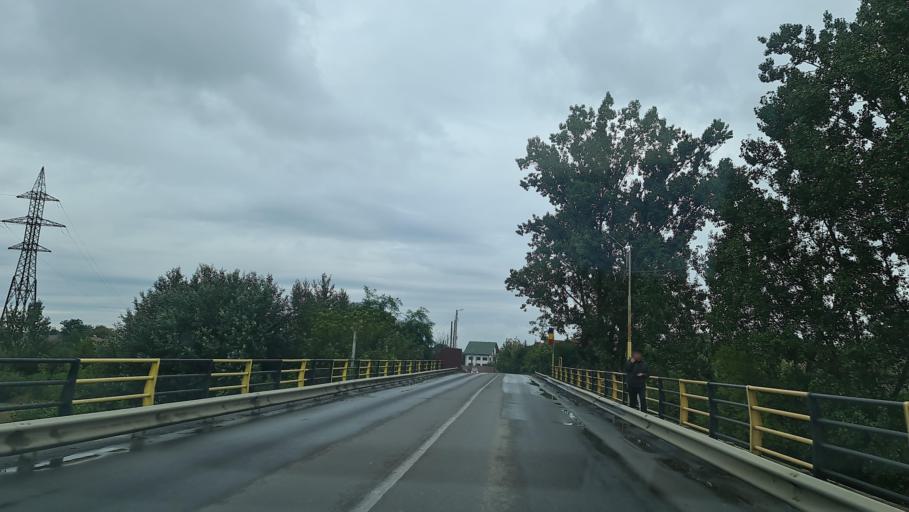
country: RO
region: Neamt
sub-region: Comuna Roznov
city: Chintinici
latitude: 46.8323
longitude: 26.4985
